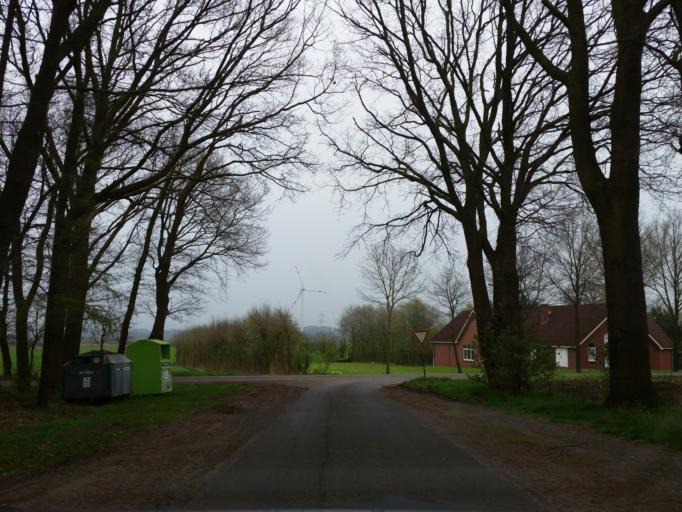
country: DE
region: Lower Saxony
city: Alfstedt
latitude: 53.5698
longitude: 9.0396
